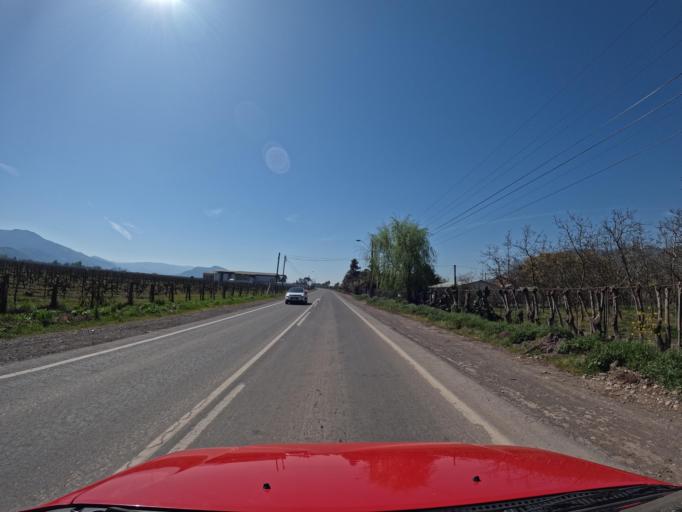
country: CL
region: Maule
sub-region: Provincia de Curico
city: Rauco
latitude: -35.0168
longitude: -71.4242
